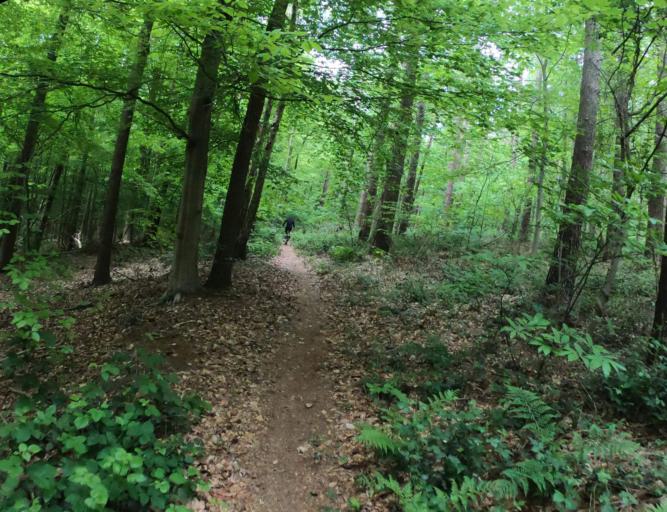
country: BE
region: Flanders
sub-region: Provincie Vlaams-Brabant
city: Beersel
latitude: 50.7388
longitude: 4.3066
